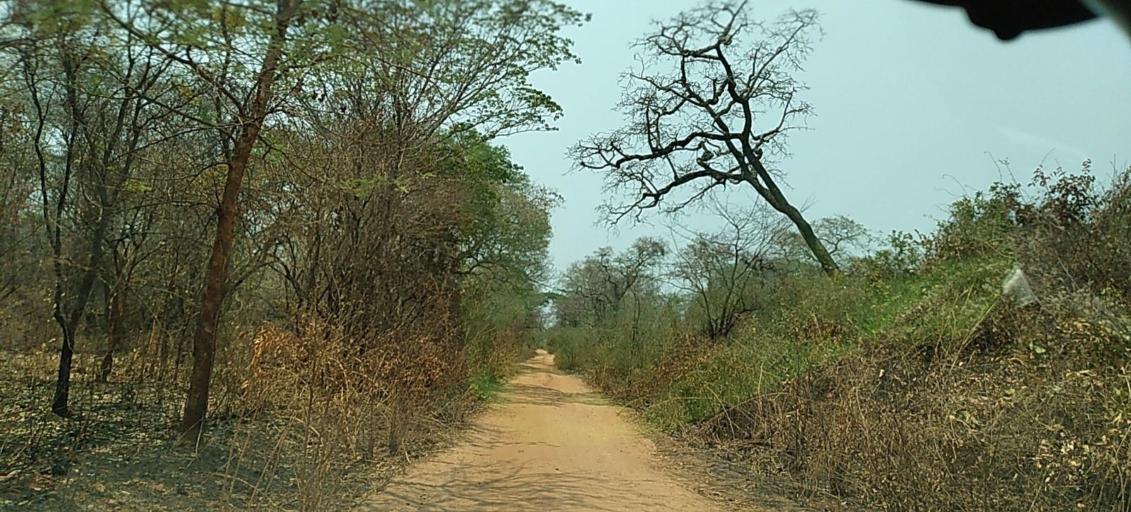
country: ZM
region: North-Western
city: Kabompo
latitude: -13.7007
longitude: 24.3173
